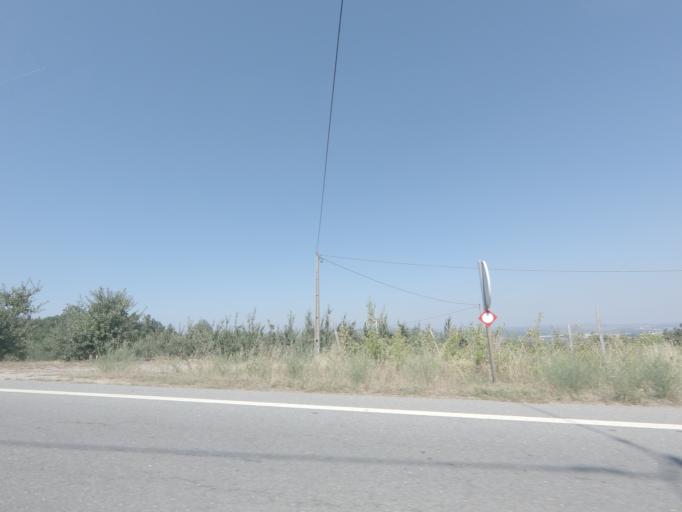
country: PT
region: Viseu
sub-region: Moimenta da Beira
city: Moimenta da Beira
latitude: 41.0041
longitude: -7.6665
